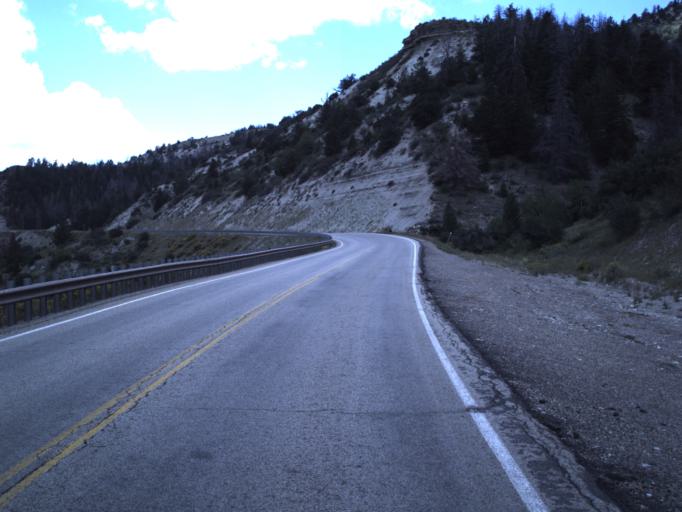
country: US
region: Utah
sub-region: Carbon County
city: Helper
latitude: 39.9026
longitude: -110.7283
